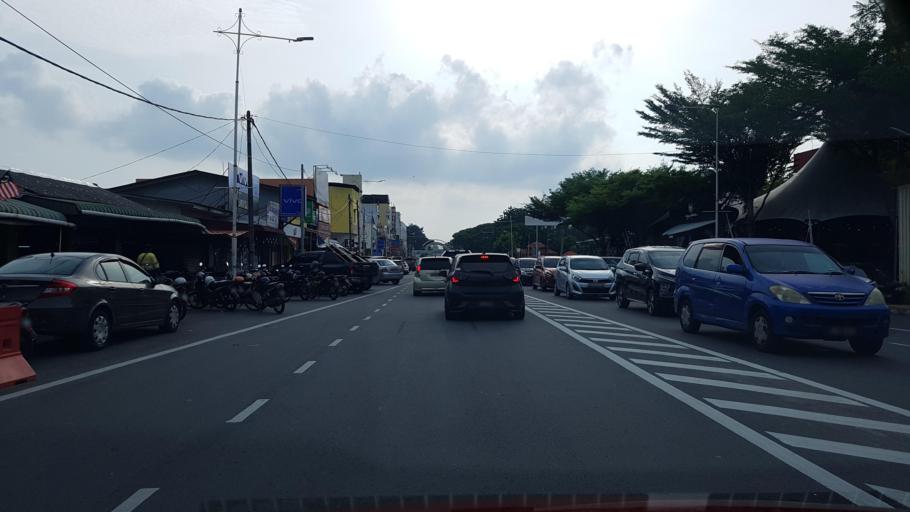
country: MY
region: Terengganu
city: Kuala Terengganu
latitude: 5.3366
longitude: 103.1421
